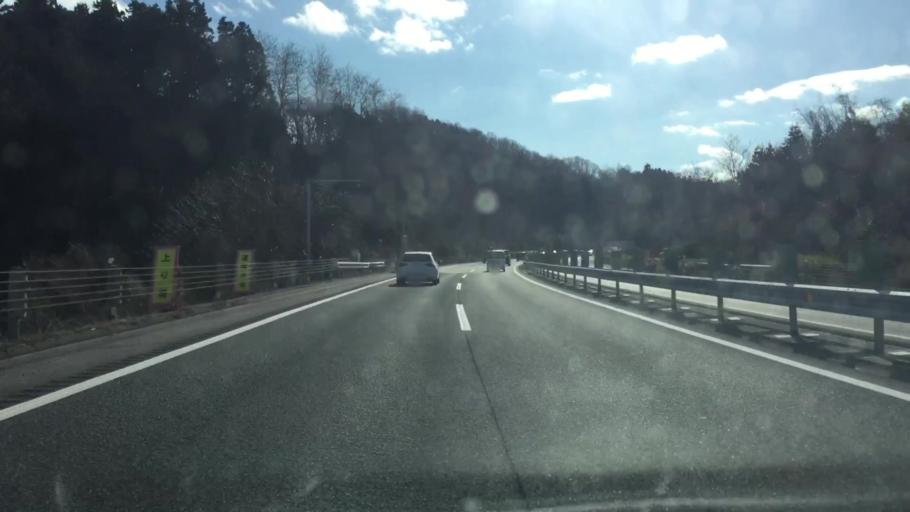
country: JP
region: Gunma
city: Numata
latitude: 36.6416
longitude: 139.0794
